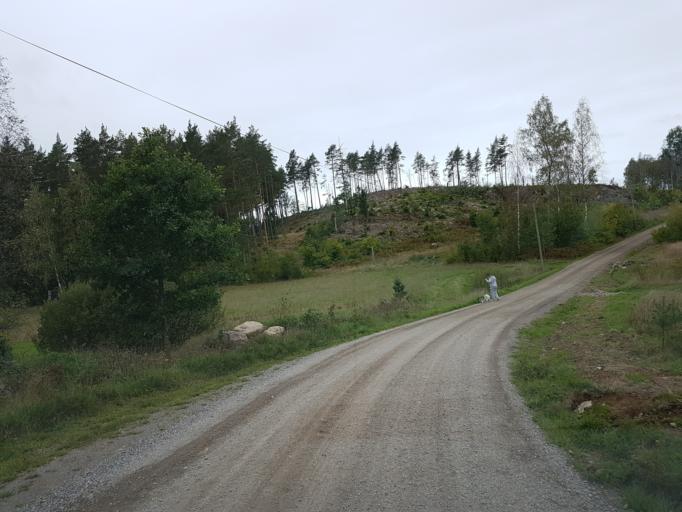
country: SE
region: OEstergoetland
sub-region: Atvidabergs Kommun
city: Atvidaberg
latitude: 58.2131
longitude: 16.0387
